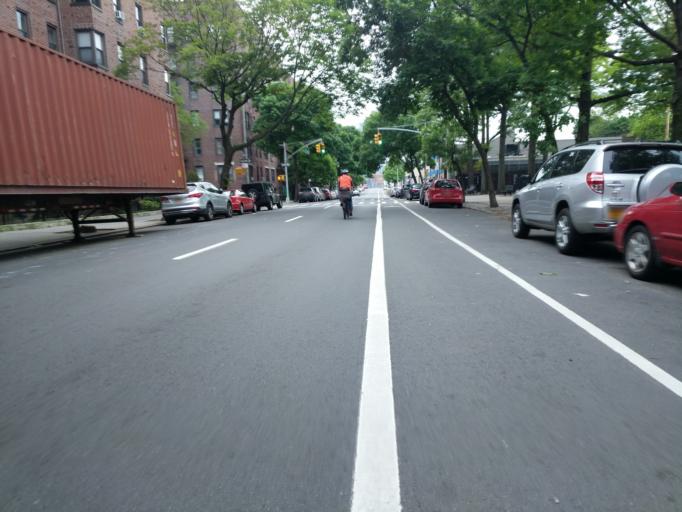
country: US
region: New York
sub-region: Queens County
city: Long Island City
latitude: 40.7470
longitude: -73.9220
